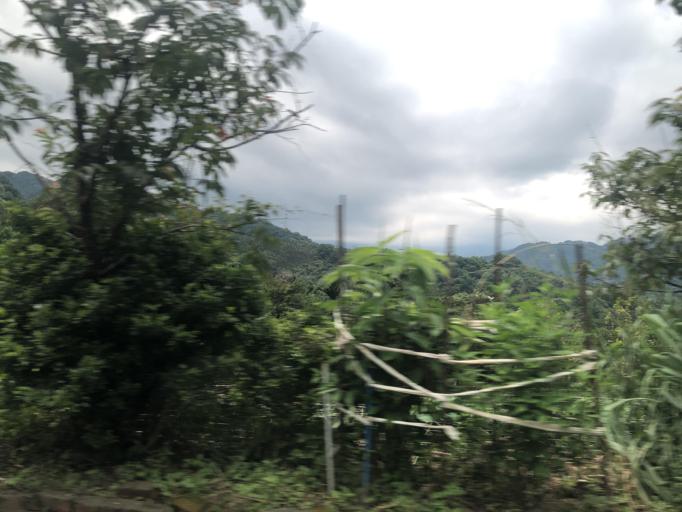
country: TW
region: Taiwan
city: Daxi
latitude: 24.8755
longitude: 121.4143
